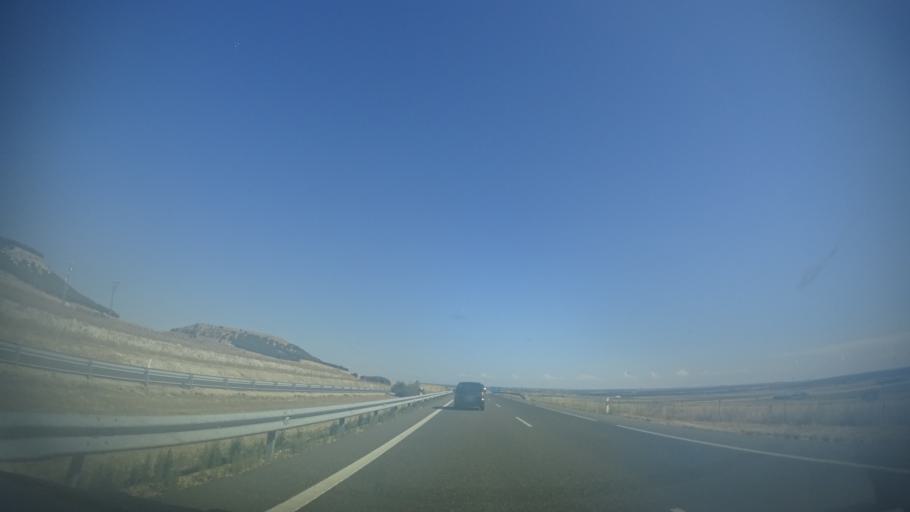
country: ES
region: Castille and Leon
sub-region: Provincia de Valladolid
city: Bercero
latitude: 41.5329
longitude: -5.0582
